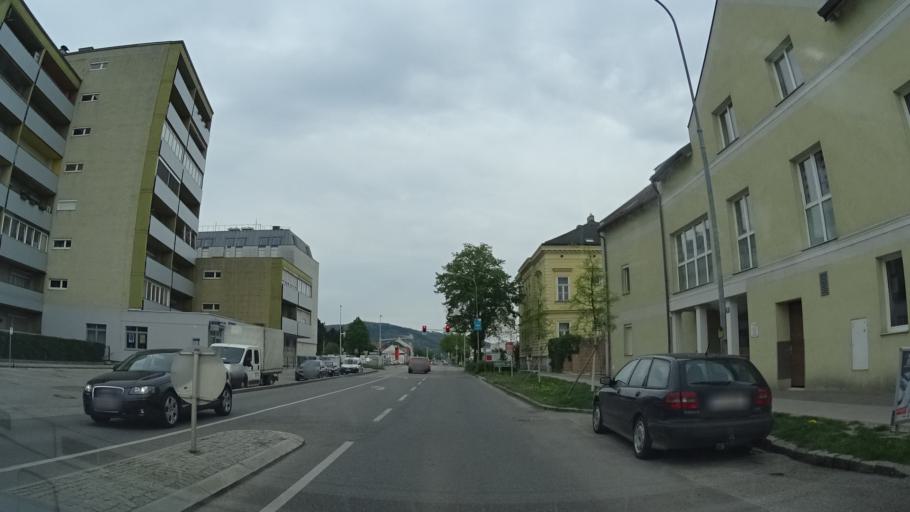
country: AT
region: Lower Austria
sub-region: Politischer Bezirk Korneuburg
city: Korneuburg
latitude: 48.3411
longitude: 16.3360
